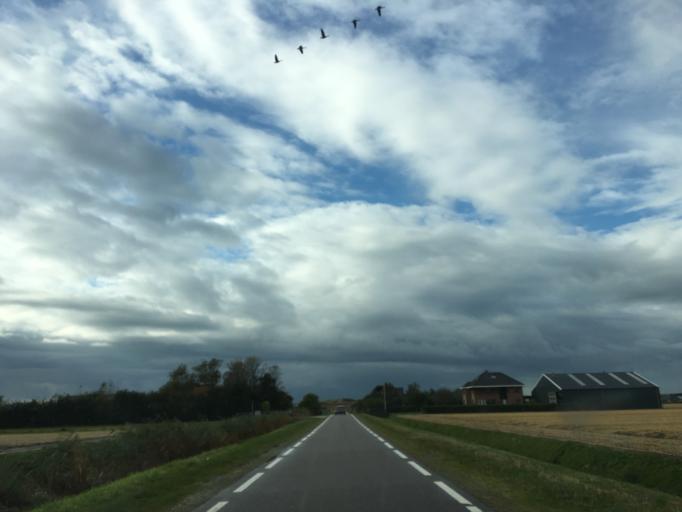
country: NL
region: North Holland
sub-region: Gemeente Den Helder
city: Den Helder
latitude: 52.9150
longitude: 4.7341
